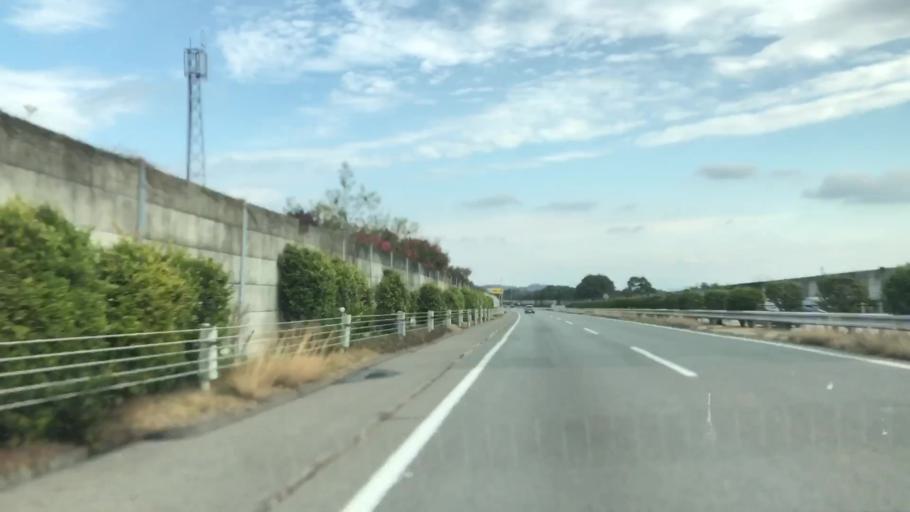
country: JP
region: Saga Prefecture
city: Kanzakimachi-kanzaki
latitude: 33.3289
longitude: 130.3018
